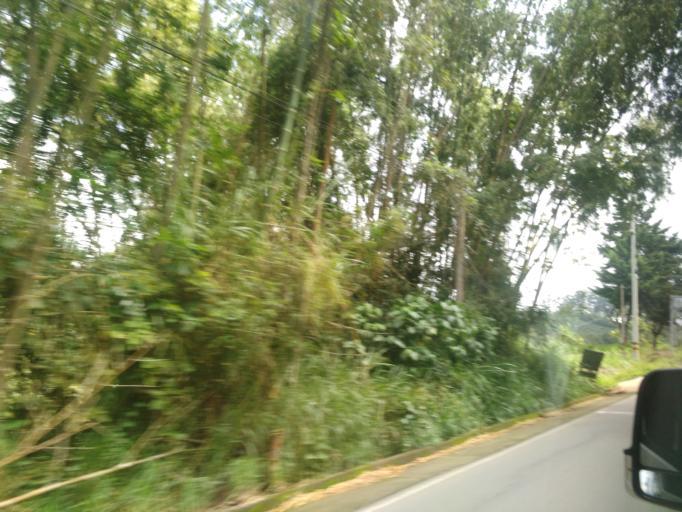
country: CO
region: Valle del Cauca
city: Sevilla
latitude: 4.2812
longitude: -75.9060
